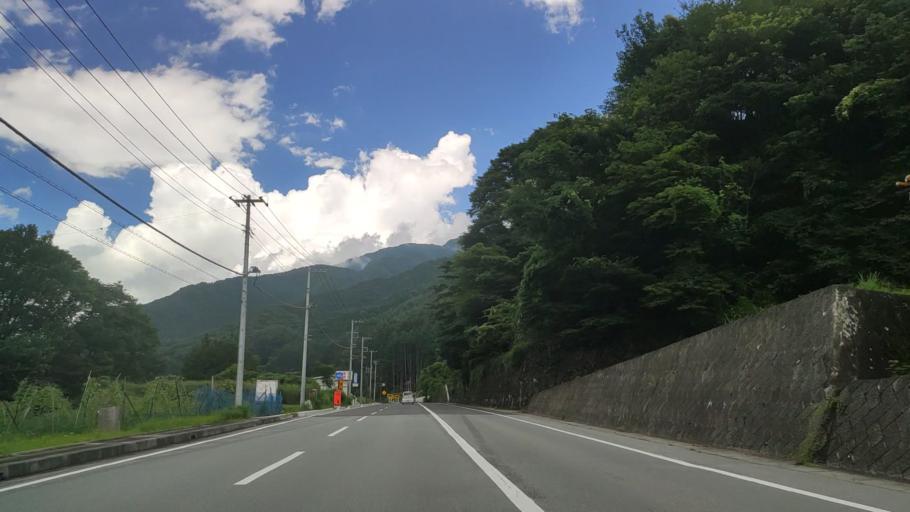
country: JP
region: Yamanashi
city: Enzan
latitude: 35.7975
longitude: 138.7445
